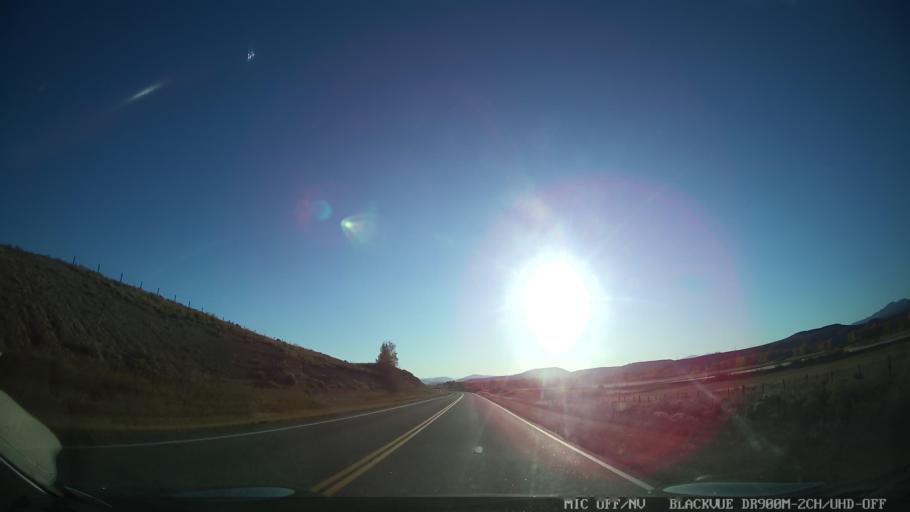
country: US
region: Colorado
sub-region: Grand County
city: Kremmling
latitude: 40.0567
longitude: -106.3188
